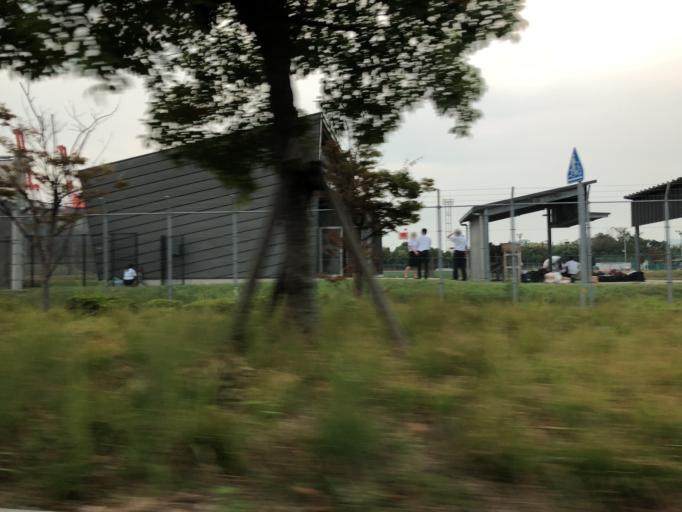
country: JP
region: Hyogo
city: Ashiya
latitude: 34.6818
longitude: 135.2683
